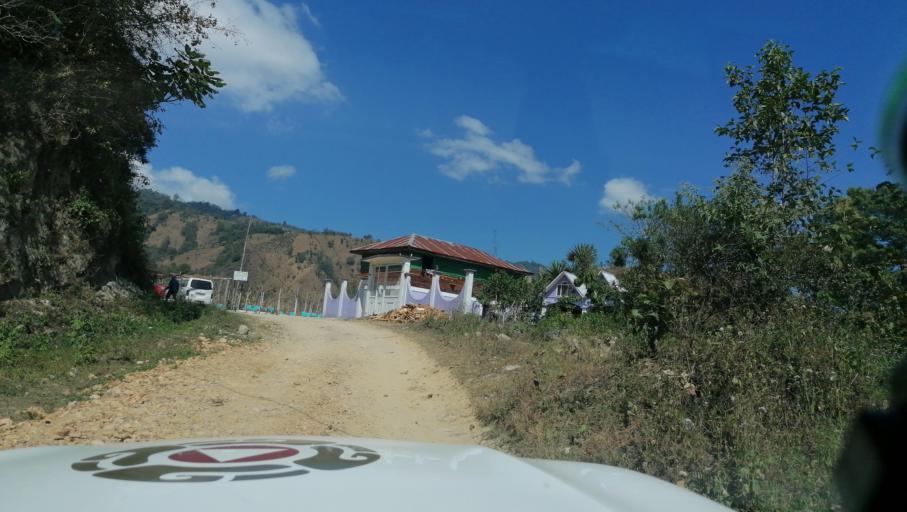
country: GT
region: San Marcos
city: Tacana
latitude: 15.2071
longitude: -92.2065
